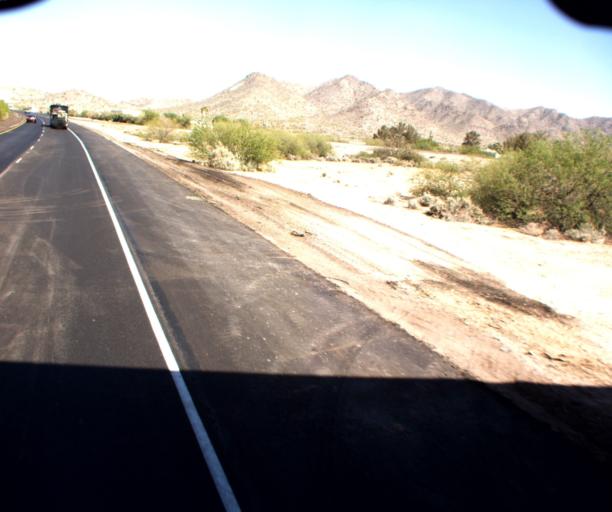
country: US
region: Arizona
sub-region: Pinal County
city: Casa Grande
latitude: 32.8283
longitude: -111.7401
